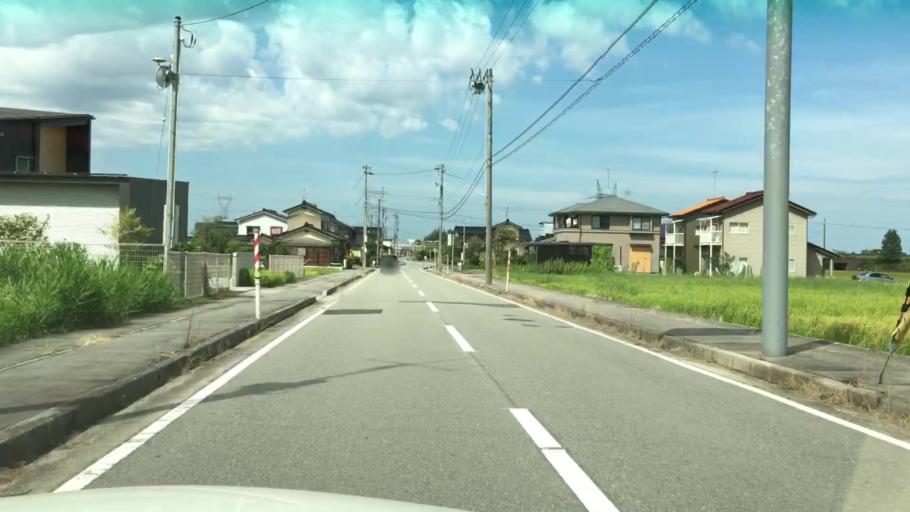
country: JP
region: Toyama
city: Kamiichi
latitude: 36.7061
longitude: 137.3412
